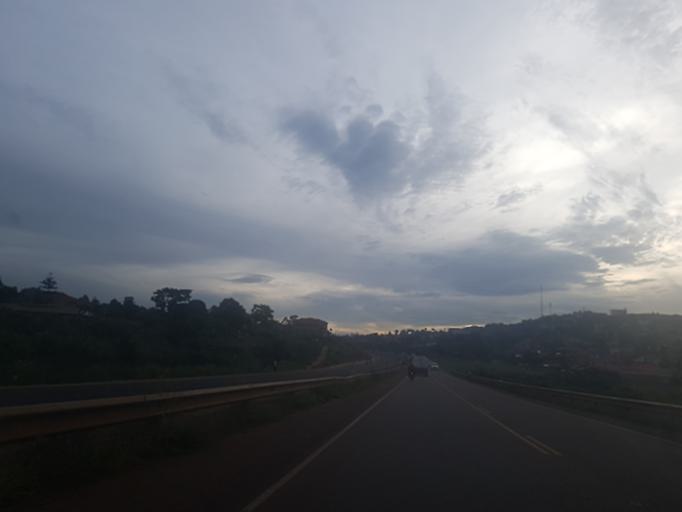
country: UG
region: Central Region
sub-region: Wakiso District
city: Kireka
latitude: 0.3688
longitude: 32.6189
